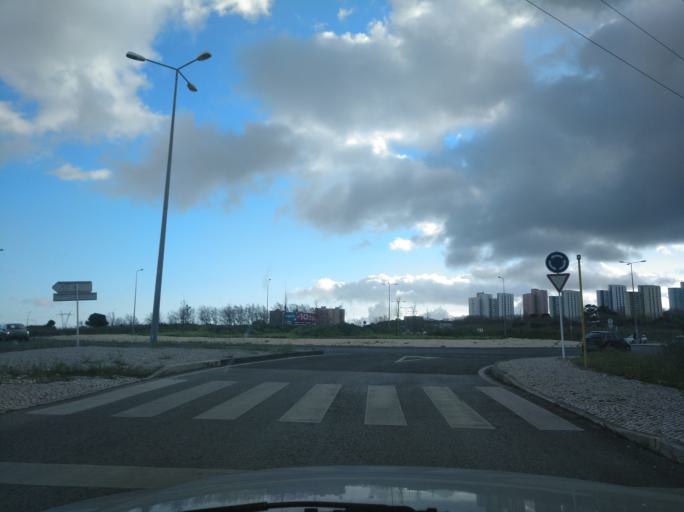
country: PT
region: Lisbon
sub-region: Loures
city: Loures
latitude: 38.8173
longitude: -9.1738
